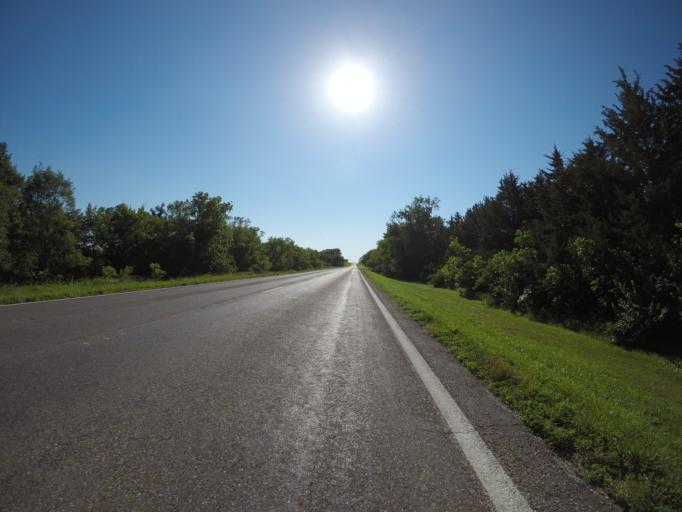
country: US
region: Kansas
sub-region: Lyon County
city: Emporia
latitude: 38.6588
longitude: -96.1729
